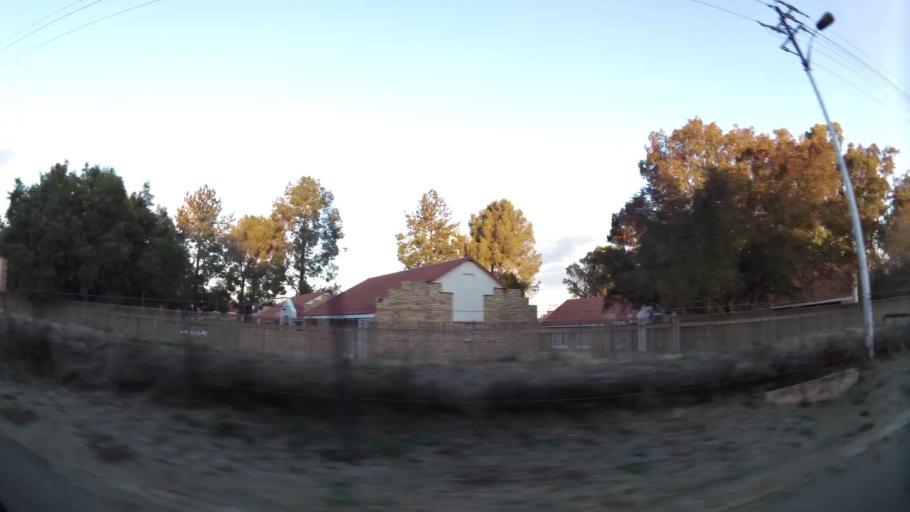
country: ZA
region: North-West
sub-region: Dr Kenneth Kaunda District Municipality
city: Potchefstroom
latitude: -26.6893
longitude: 27.0864
